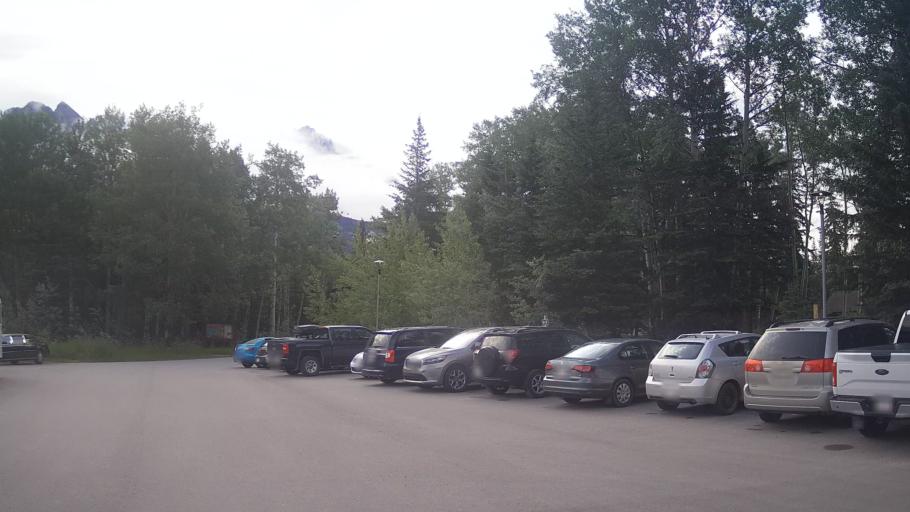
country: CA
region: Alberta
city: Jasper Park Lodge
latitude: 52.9643
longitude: -118.0597
